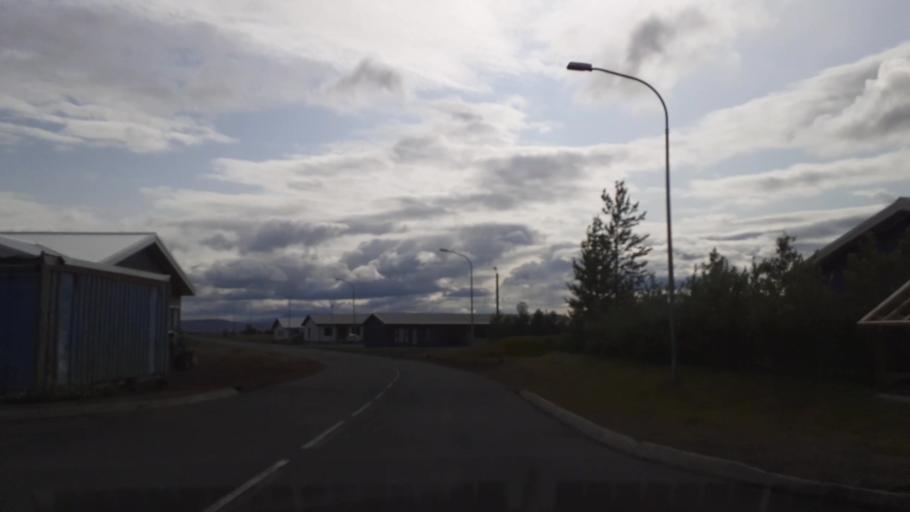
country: IS
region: South
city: Vestmannaeyjar
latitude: 63.8331
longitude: -20.3875
